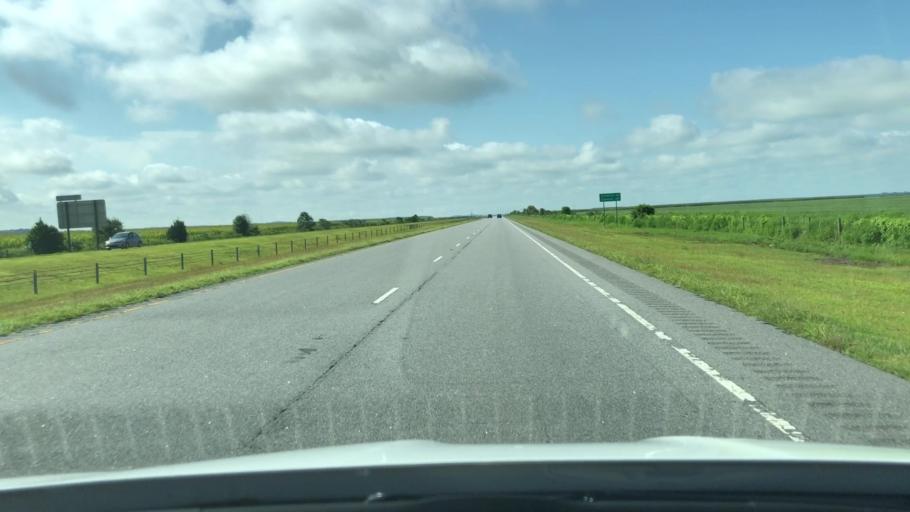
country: US
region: North Carolina
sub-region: Pasquotank County
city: Elizabeth City
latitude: 36.3545
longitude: -76.3149
